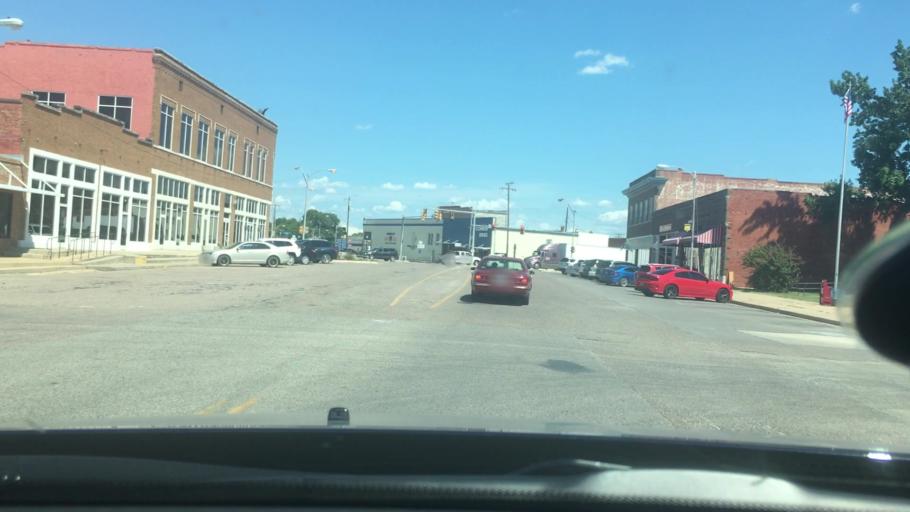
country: US
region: Oklahoma
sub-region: Marshall County
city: Madill
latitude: 34.0906
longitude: -96.7732
